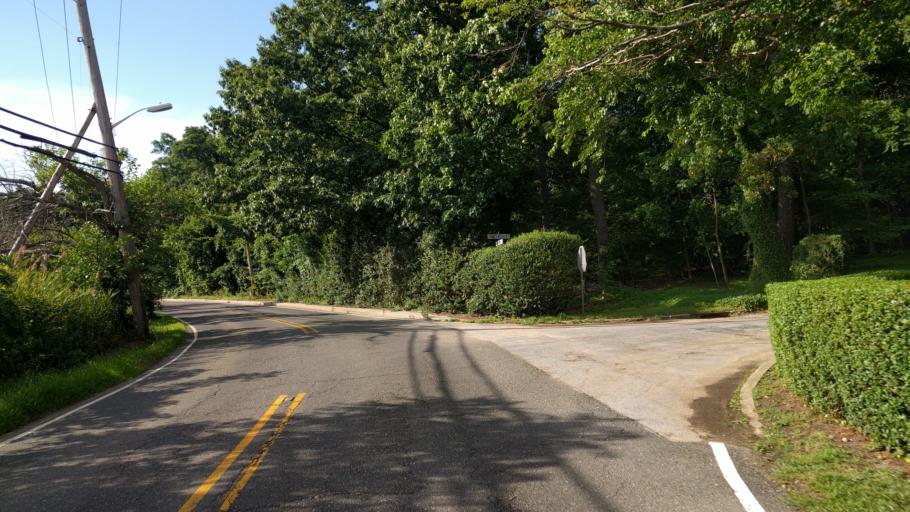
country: US
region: New York
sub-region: Nassau County
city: Oyster Bay Cove
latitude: 40.8798
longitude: -73.5044
